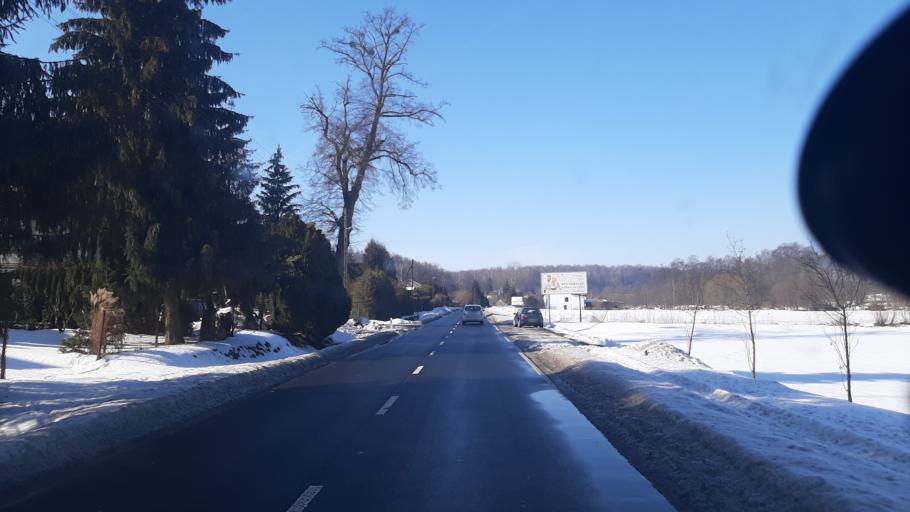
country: PL
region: Lublin Voivodeship
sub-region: Powiat pulawski
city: Wawolnica
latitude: 51.2835
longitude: 22.1780
